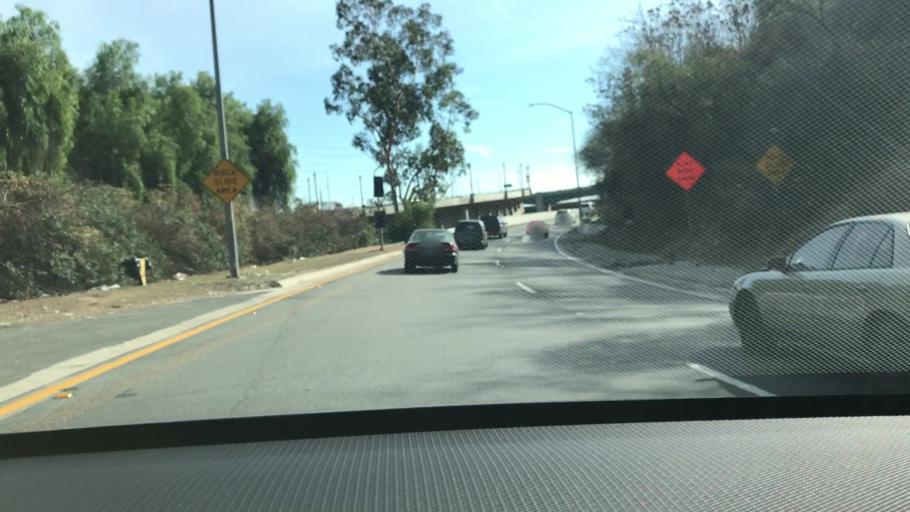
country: US
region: California
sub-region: Los Angeles County
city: Echo Park
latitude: 34.0830
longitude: -118.2290
